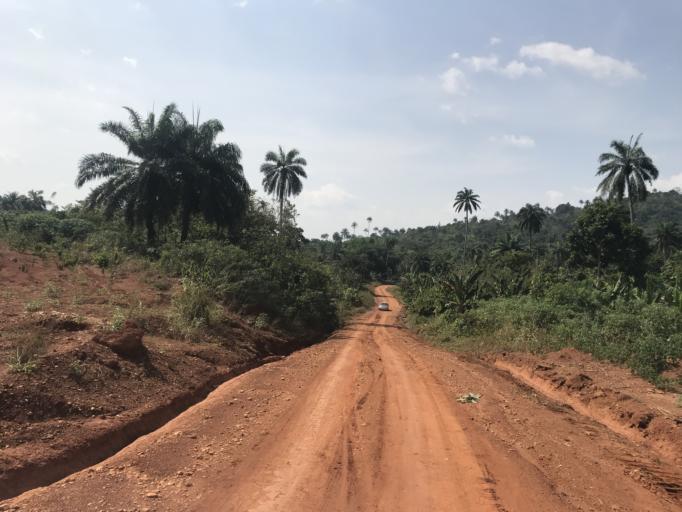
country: NG
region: Osun
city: Ilesa
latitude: 7.6295
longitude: 4.6891
